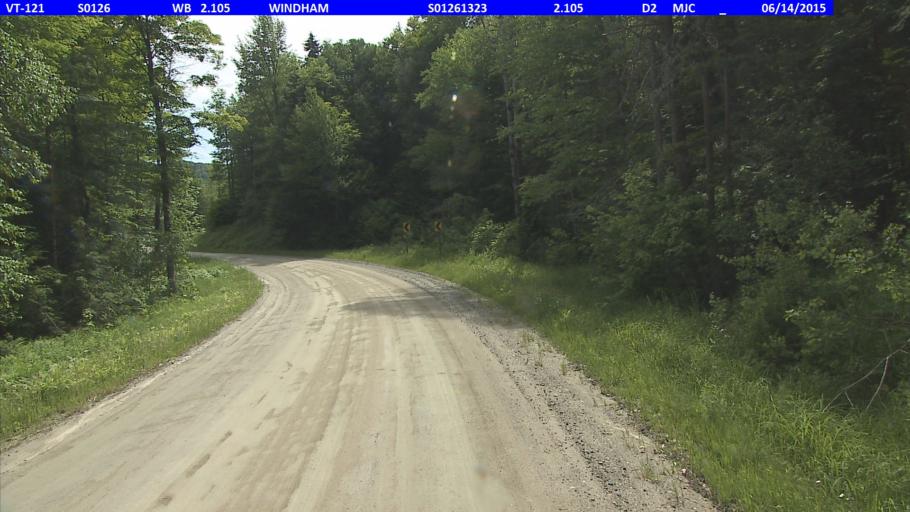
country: US
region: Vermont
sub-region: Windsor County
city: Chester
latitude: 43.1986
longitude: -72.6830
